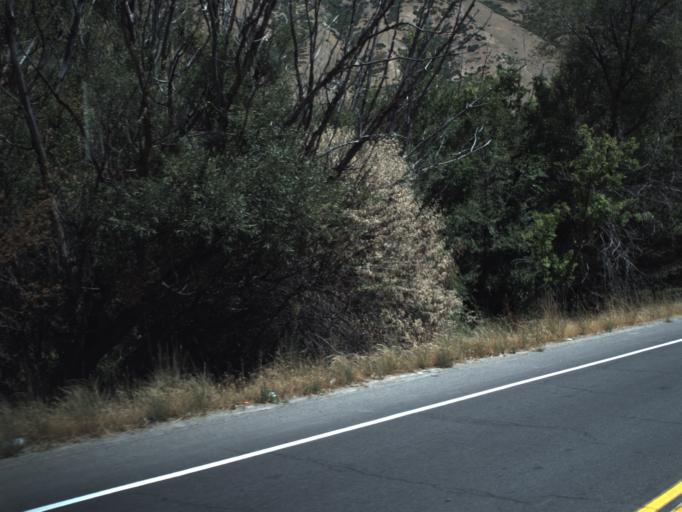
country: US
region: Utah
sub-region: Utah County
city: Springville
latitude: 40.1857
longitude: -111.6149
